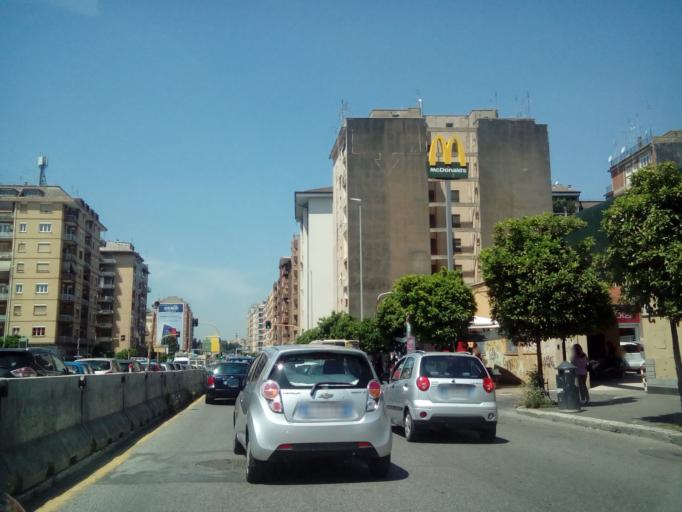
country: IT
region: Latium
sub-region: Citta metropolitana di Roma Capitale
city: Rome
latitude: 41.9087
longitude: 12.5409
